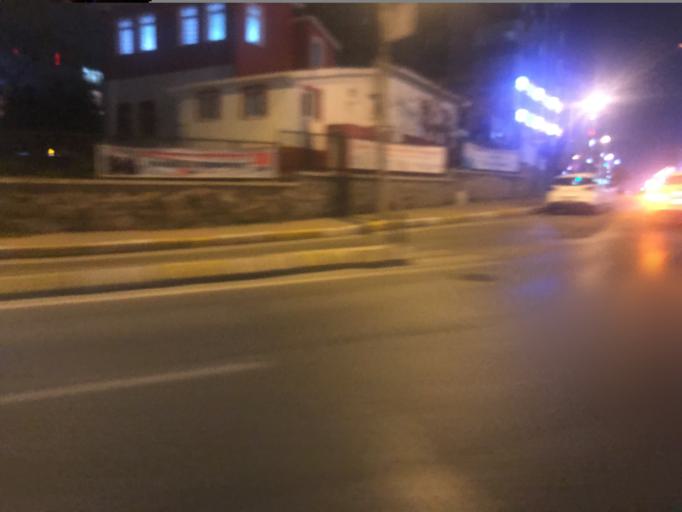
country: TR
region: Istanbul
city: Bahcelievler
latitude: 40.9781
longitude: 28.8686
